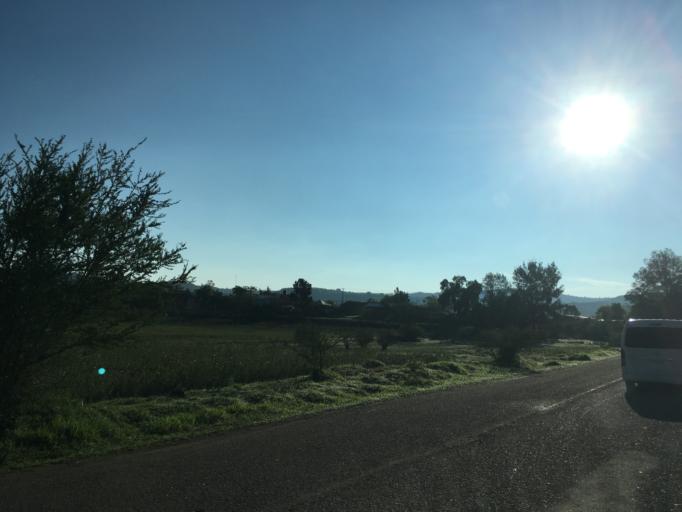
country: MX
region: Oaxaca
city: Santiago Tillo
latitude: 17.5313
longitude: -97.3455
